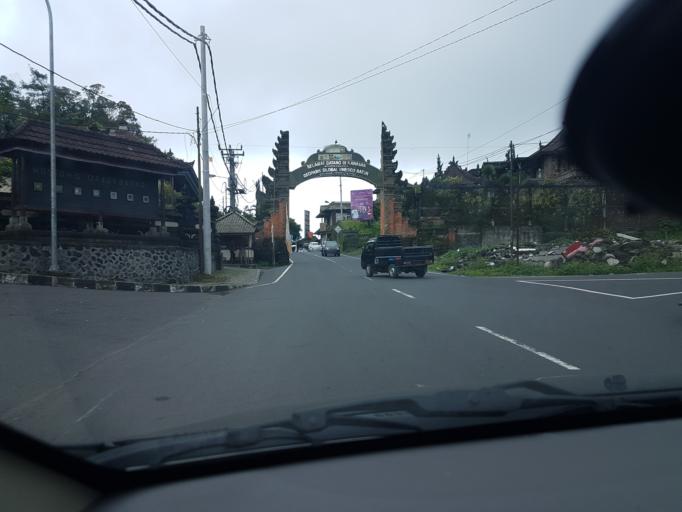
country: ID
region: Bali
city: Banjar Kedisan
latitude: -8.2844
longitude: 115.3651
